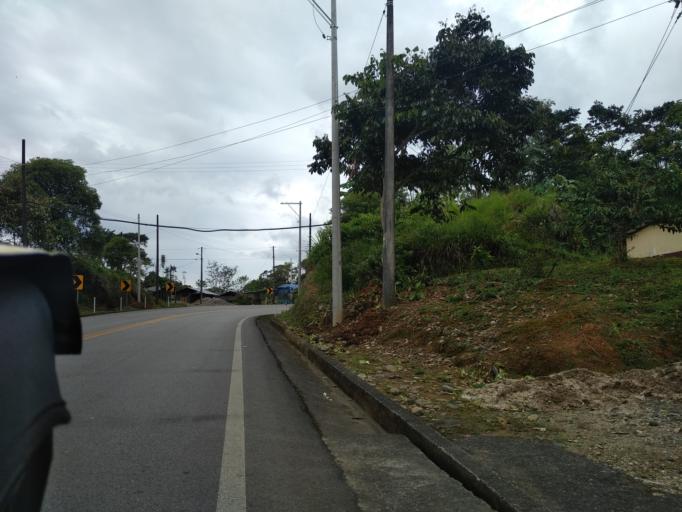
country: EC
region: Pastaza
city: Puyo
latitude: -1.3325
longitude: -77.9001
